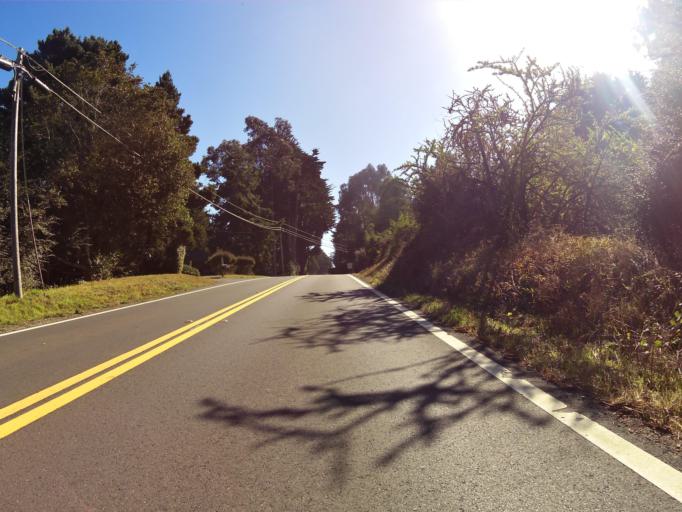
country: US
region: California
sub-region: Mendocino County
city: Fort Bragg
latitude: 39.5216
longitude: -123.7614
